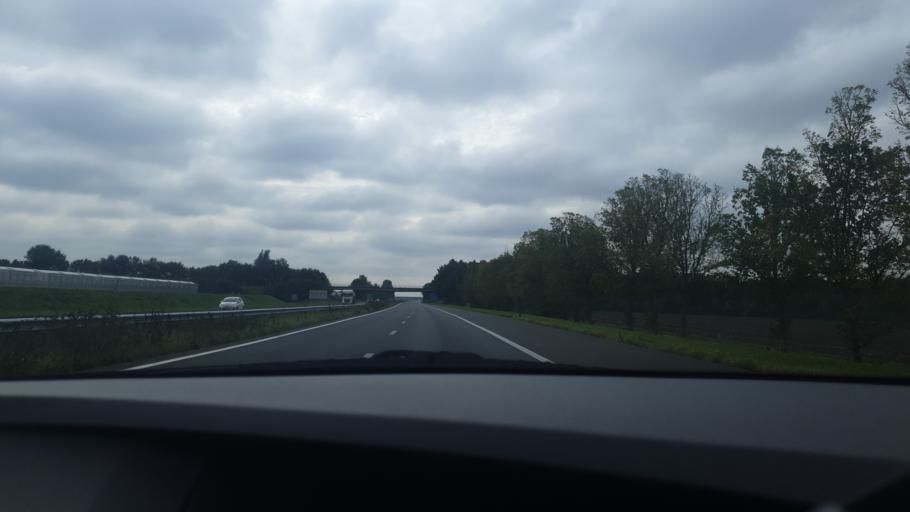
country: NL
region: North Brabant
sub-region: Gemeente Steenbergen
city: Dinteloord
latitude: 51.6347
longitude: 4.3882
